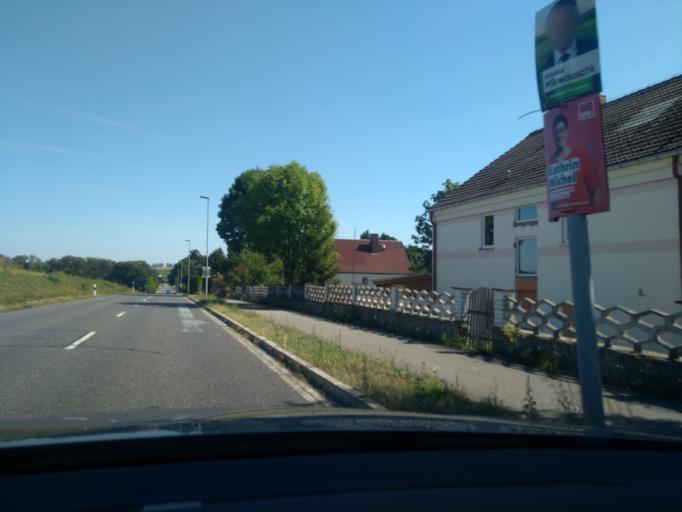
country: DE
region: Saxony
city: Crostwitz
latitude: 51.2195
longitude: 14.2493
